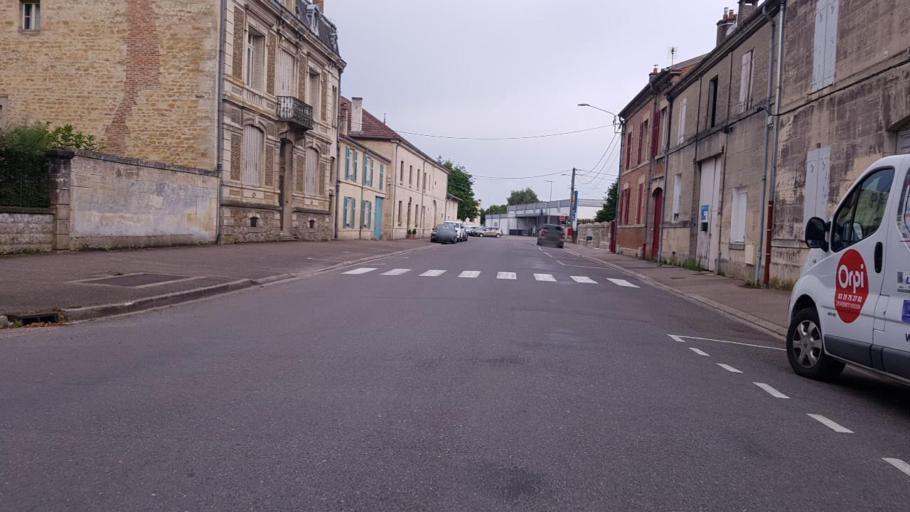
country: FR
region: Lorraine
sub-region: Departement de la Meuse
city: Revigny-sur-Ornain
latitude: 48.8275
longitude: 4.9842
